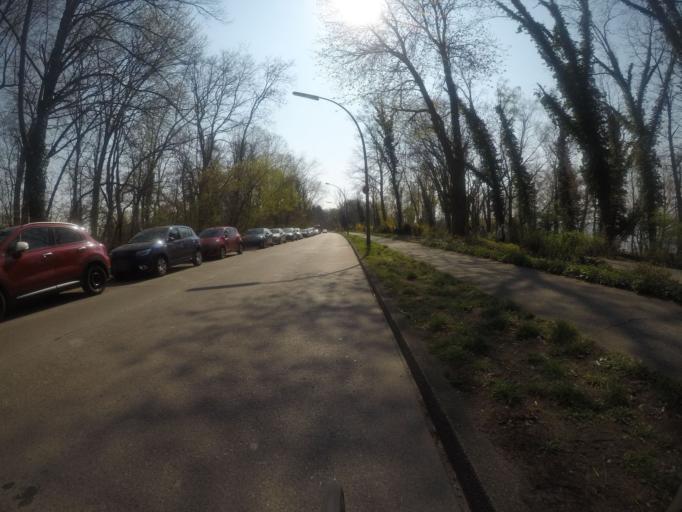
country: DE
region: Berlin
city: Tegel
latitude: 52.5834
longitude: 13.2753
